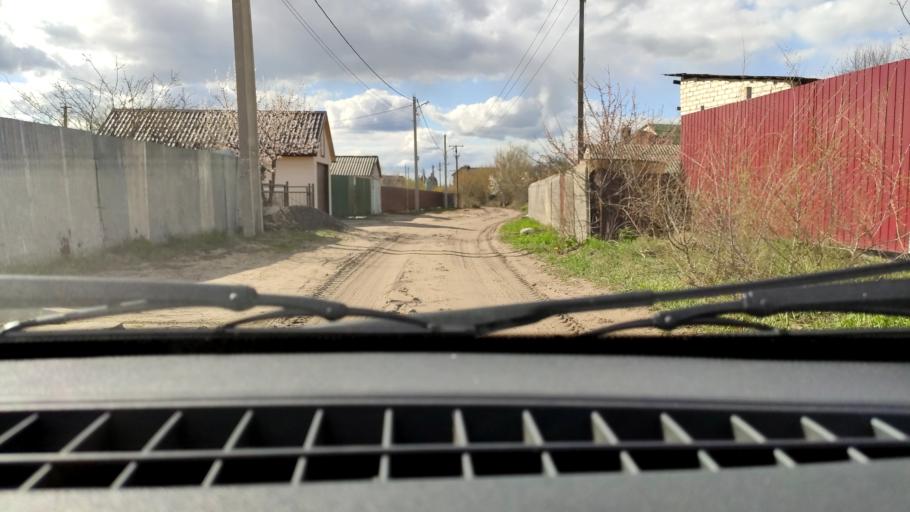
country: RU
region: Voronezj
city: Podgornoye
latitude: 51.7347
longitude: 39.1607
